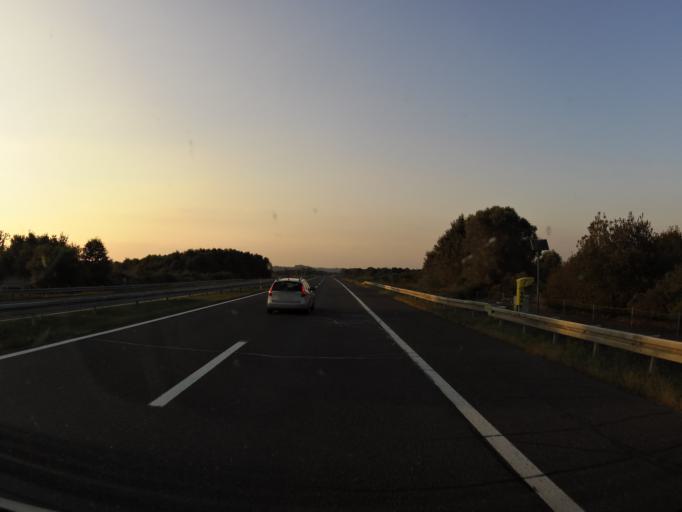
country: HR
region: Zagrebacka
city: Pojatno
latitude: 45.8890
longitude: 15.8259
